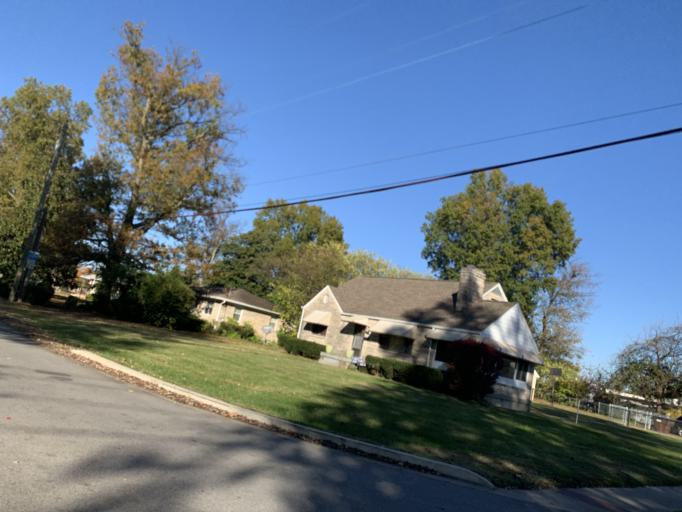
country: US
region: Kentucky
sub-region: Jefferson County
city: Saint Dennis
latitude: 38.1686
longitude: -85.8302
